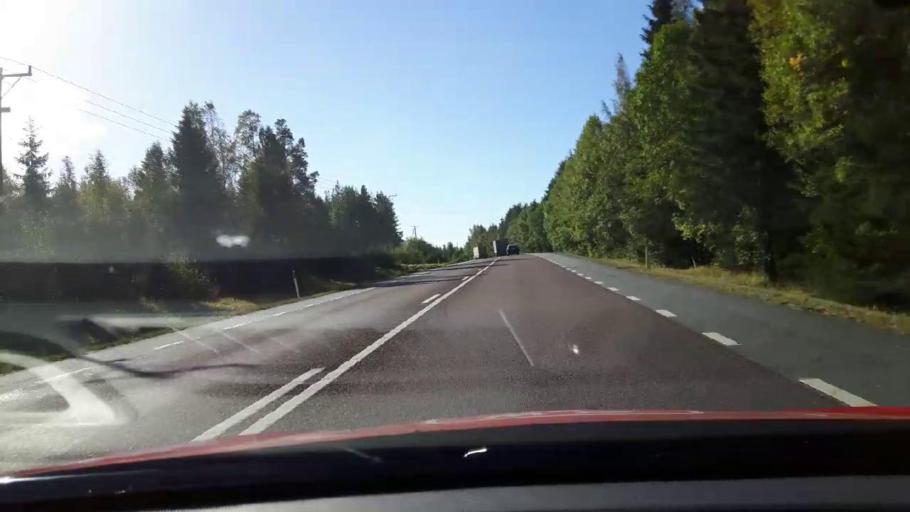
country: SE
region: Jaemtland
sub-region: Braecke Kommun
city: Braecke
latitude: 62.7820
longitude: 15.3853
